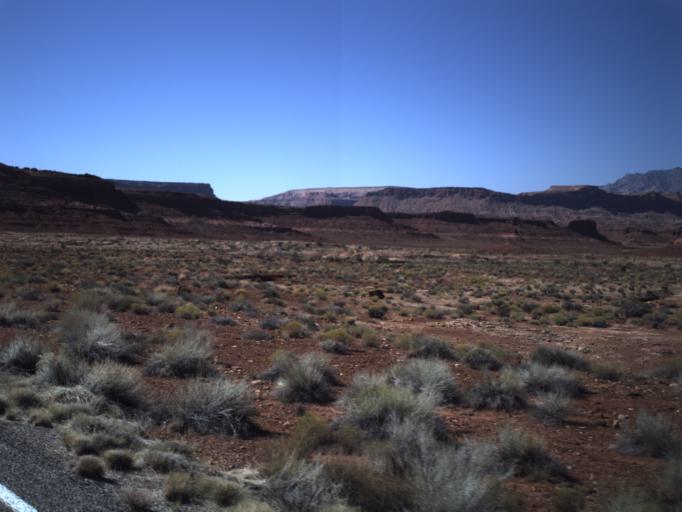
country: US
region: Utah
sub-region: San Juan County
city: Blanding
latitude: 37.8349
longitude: -110.3572
